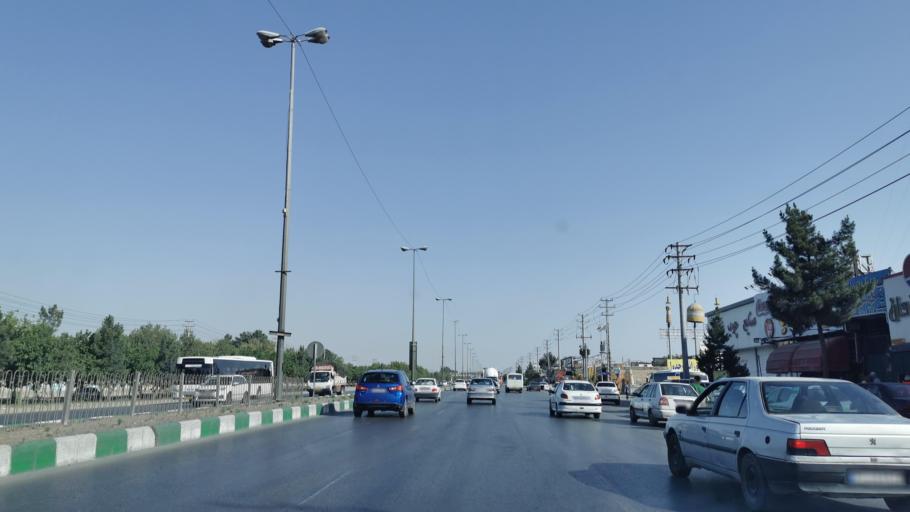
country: IR
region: Razavi Khorasan
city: Mashhad
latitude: 36.4088
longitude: 59.4748
